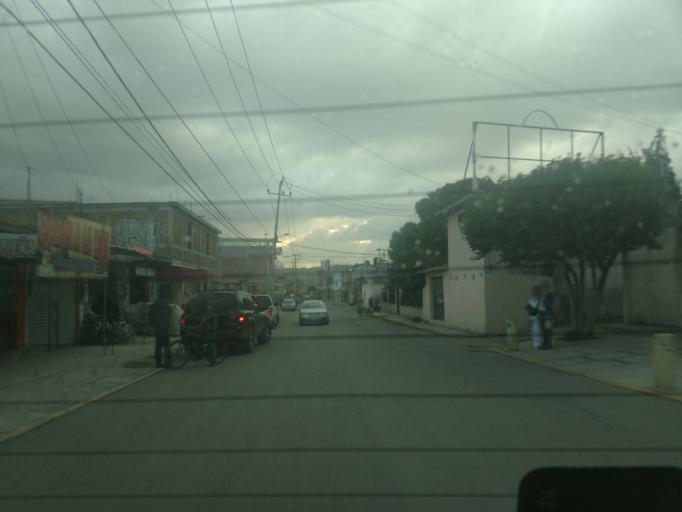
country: MX
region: Morelos
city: Coyotepec
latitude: 19.7772
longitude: -99.2152
